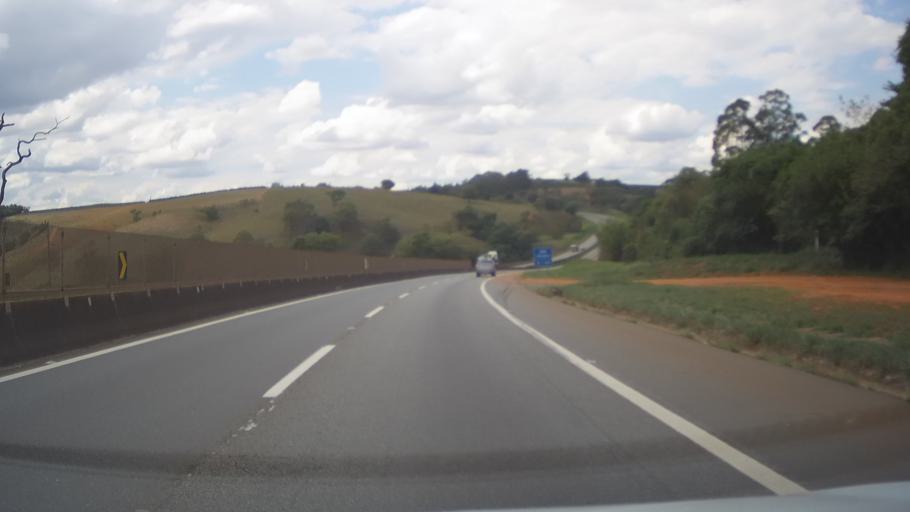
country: BR
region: Minas Gerais
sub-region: Nepomuceno
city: Nepomuceno
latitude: -21.2777
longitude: -45.1396
